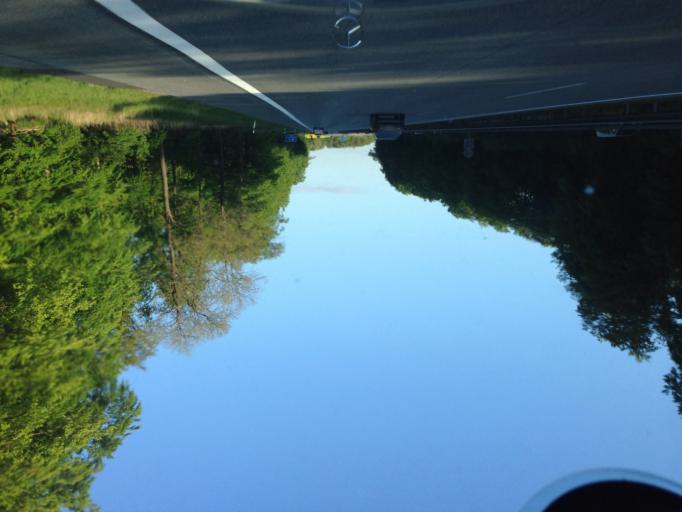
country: DE
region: Schleswig-Holstein
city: Politz
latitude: 53.7735
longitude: 10.4020
